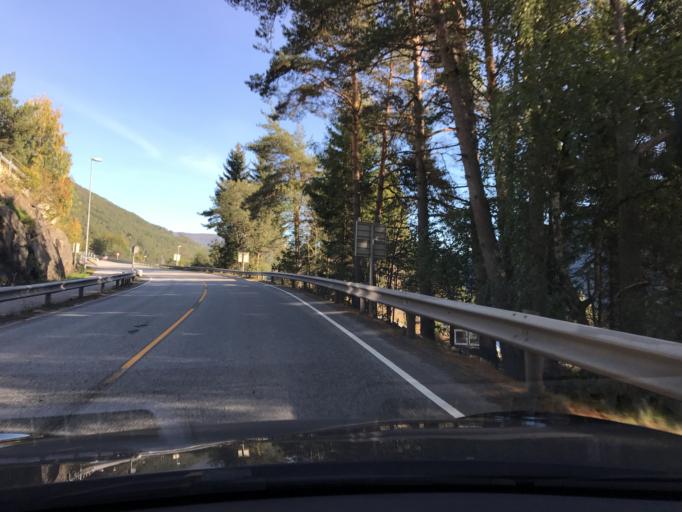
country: NO
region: Sogn og Fjordane
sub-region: Sogndal
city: Sogndalsfjora
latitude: 61.2110
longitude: 7.1248
